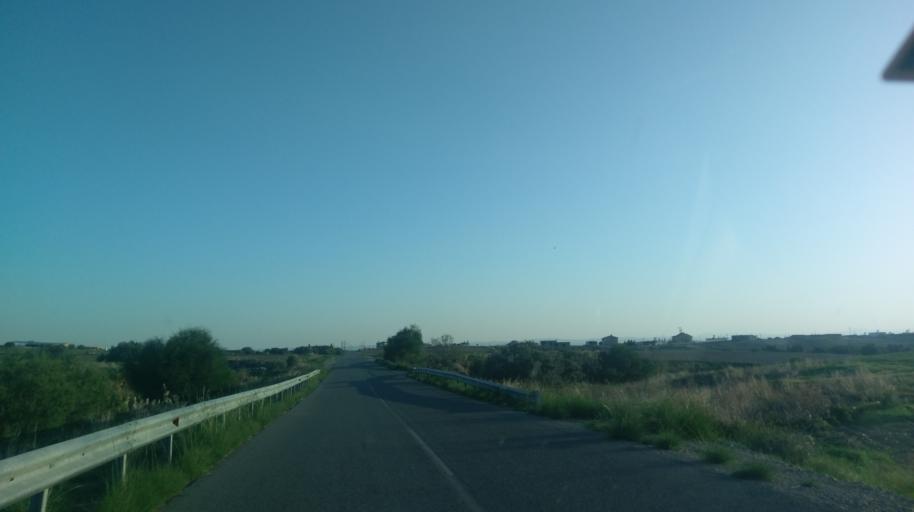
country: CY
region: Ammochostos
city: Lefkonoiko
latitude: 35.2461
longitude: 33.5530
